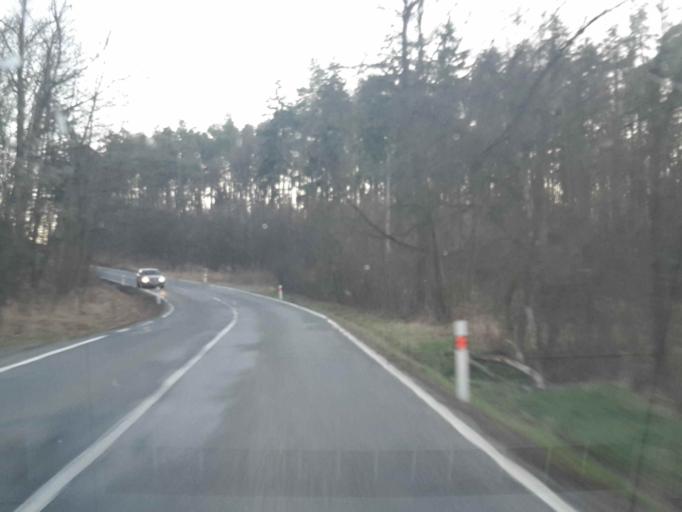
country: CZ
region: South Moravian
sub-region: Mesto Brno
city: Mokra Hora
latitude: 49.2684
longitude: 16.6287
